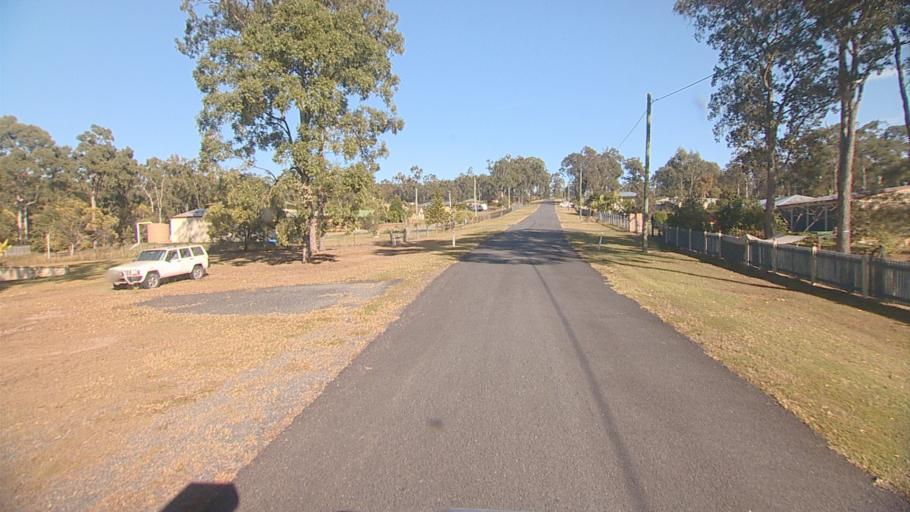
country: AU
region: Queensland
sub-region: Ipswich
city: Springfield Lakes
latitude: -27.7000
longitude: 152.9341
